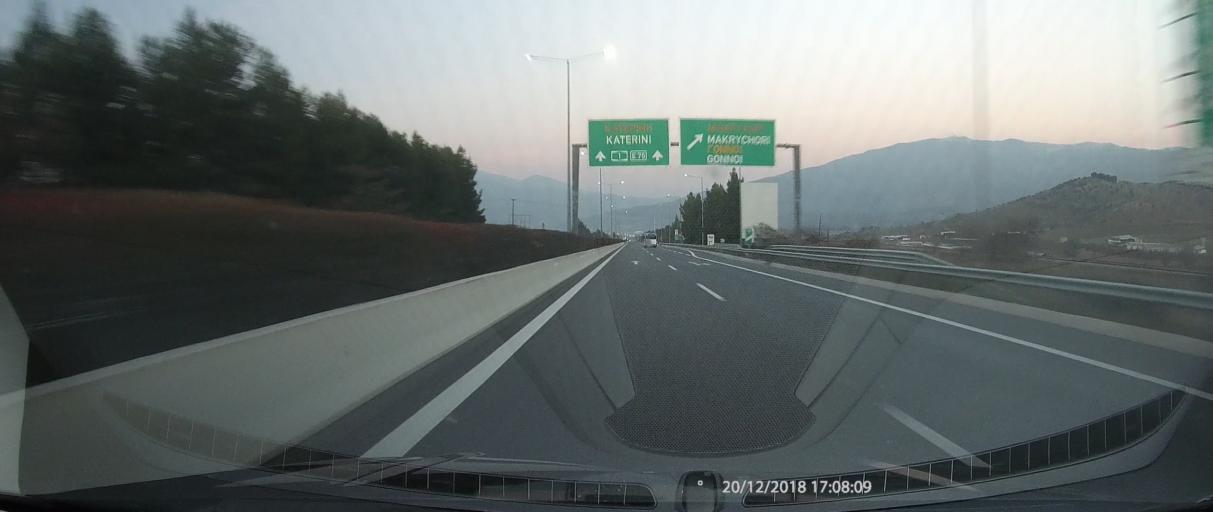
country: GR
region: Thessaly
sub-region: Nomos Larisis
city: Makrychori
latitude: 39.7926
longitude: 22.4962
